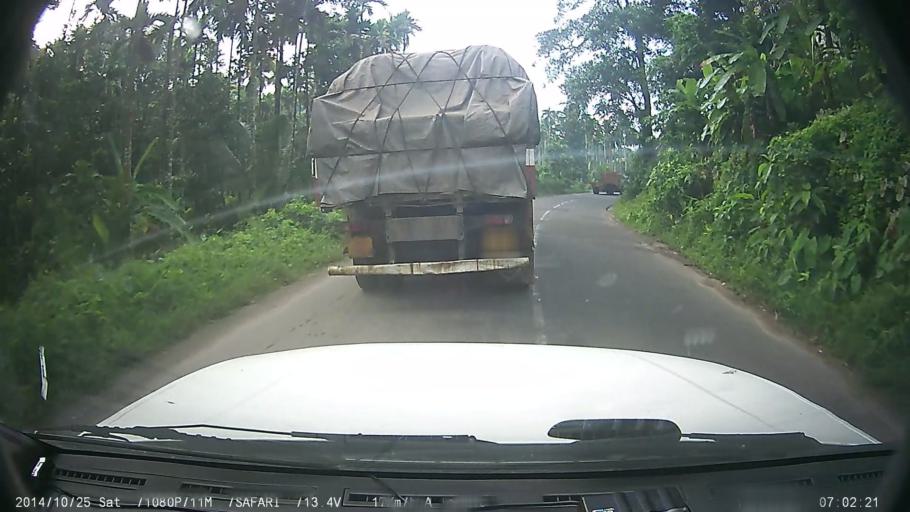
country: IN
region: Kerala
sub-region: Ernakulam
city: Piravam
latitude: 9.8748
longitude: 76.5965
